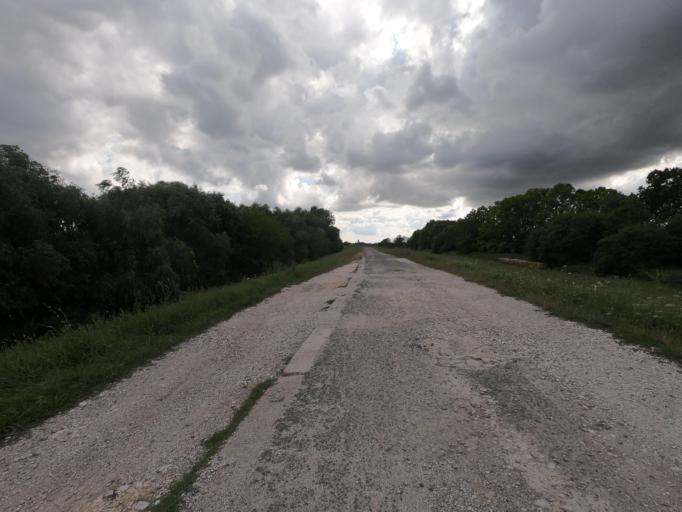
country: HU
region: Heves
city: Poroszlo
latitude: 47.6581
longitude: 20.6802
